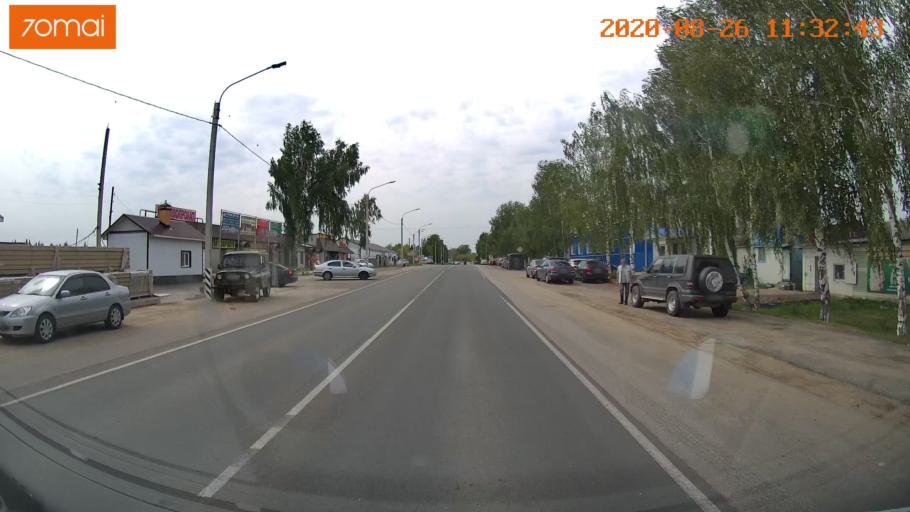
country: RU
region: Rjazan
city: Shilovo
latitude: 54.3005
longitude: 40.8622
